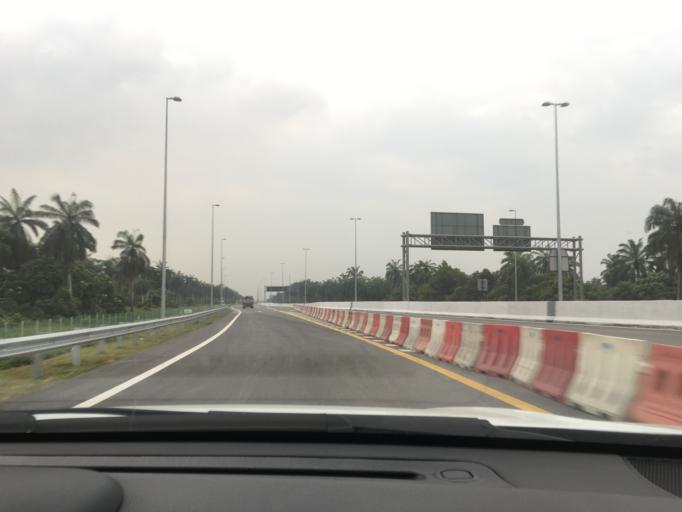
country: MY
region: Selangor
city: Klang
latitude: 3.1273
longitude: 101.4051
